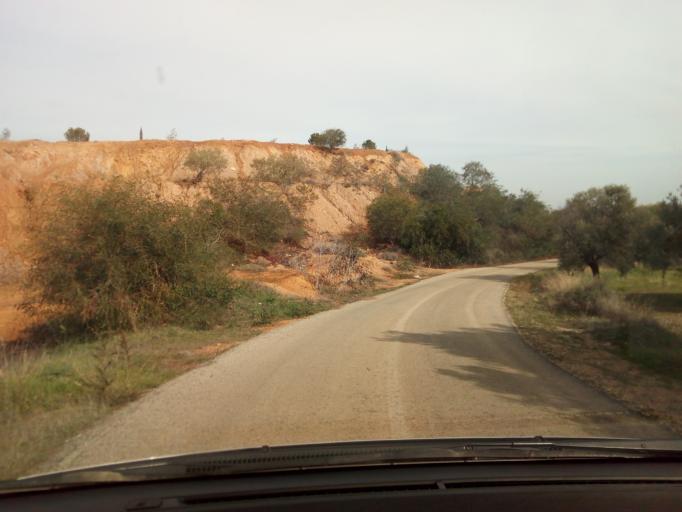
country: CY
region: Lefkosia
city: Klirou
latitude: 35.0421
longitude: 33.1466
